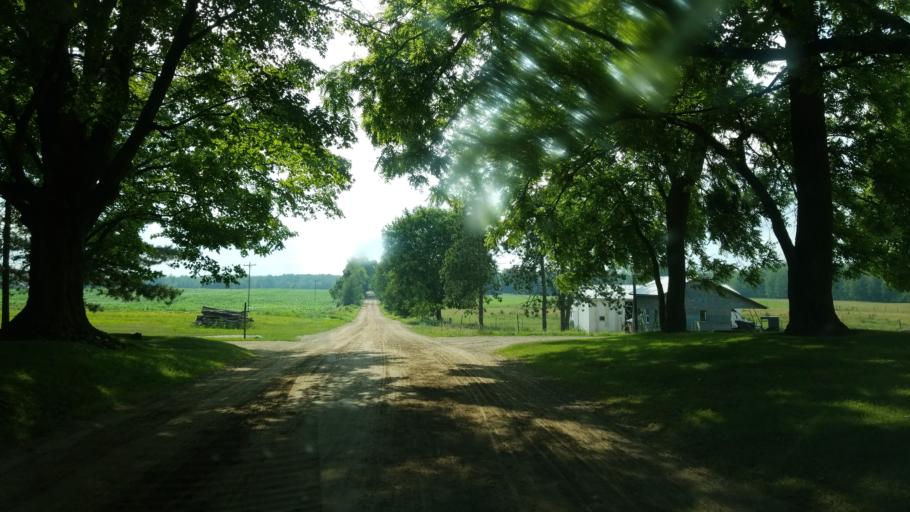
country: US
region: Michigan
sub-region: Mecosta County
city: Canadian Lakes
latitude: 43.5693
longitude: -85.3767
